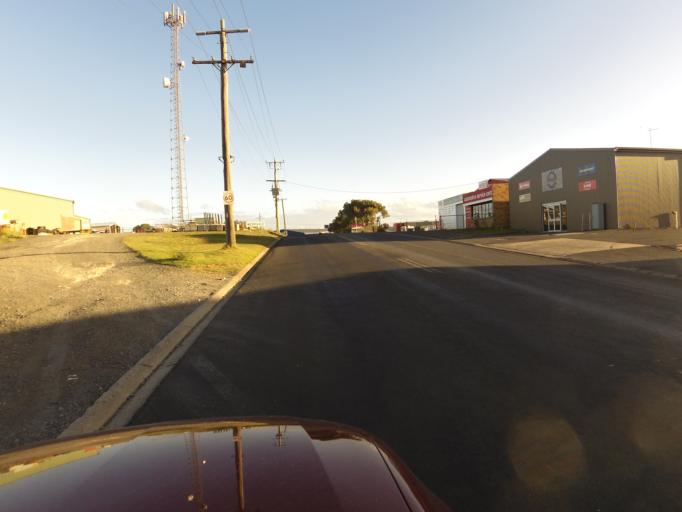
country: AU
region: Victoria
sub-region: Warrnambool
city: Warrnambool
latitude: -38.3686
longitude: 142.4589
